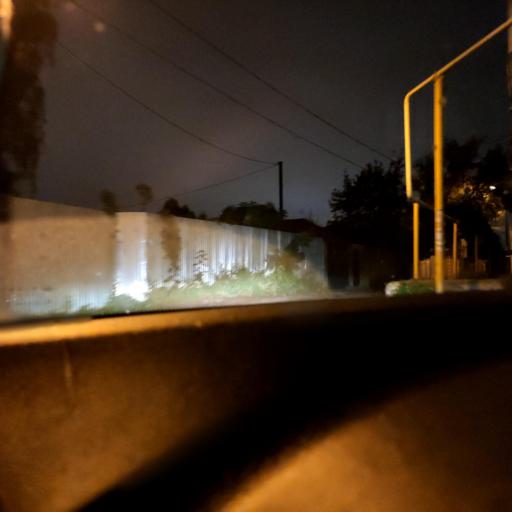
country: RU
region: Samara
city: Samara
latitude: 53.2588
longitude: 50.1849
